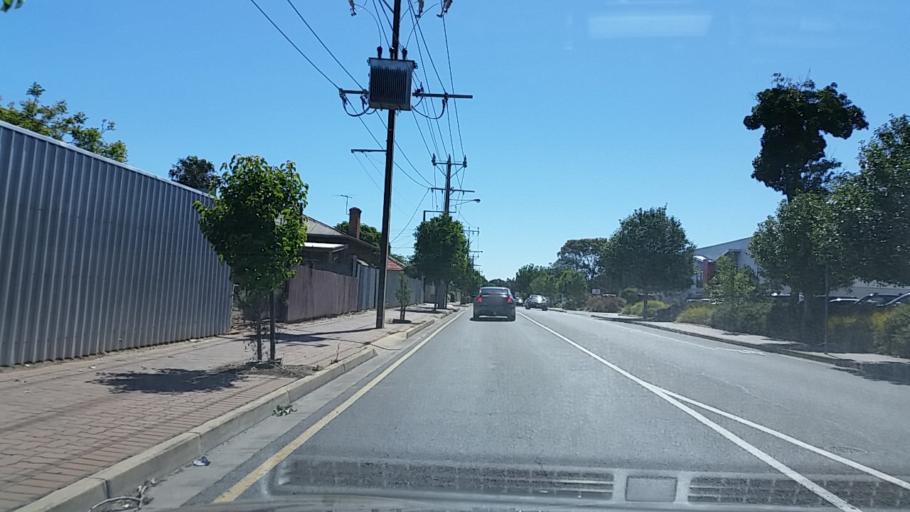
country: AU
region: South Australia
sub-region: City of West Torrens
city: Thebarton
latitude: -34.9146
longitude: 138.5602
